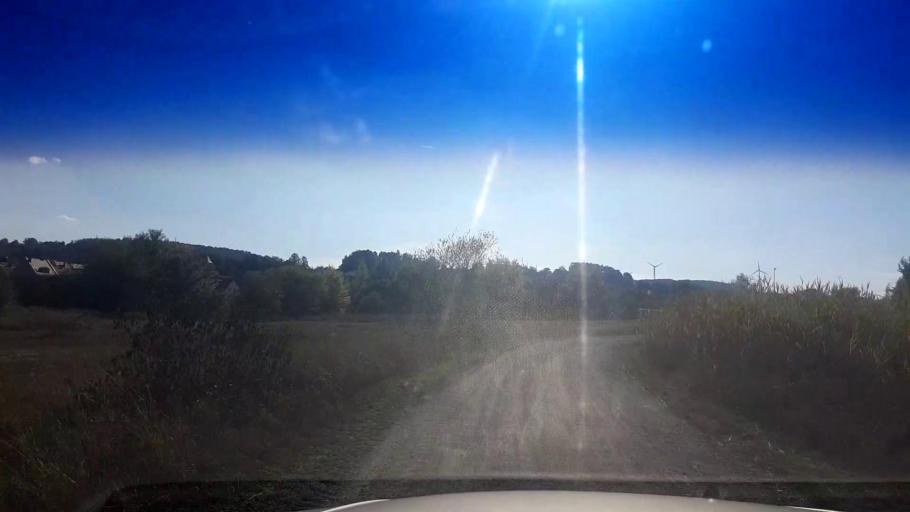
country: DE
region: Bavaria
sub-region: Upper Franconia
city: Viereth-Trunstadt
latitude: 49.9269
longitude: 10.7783
